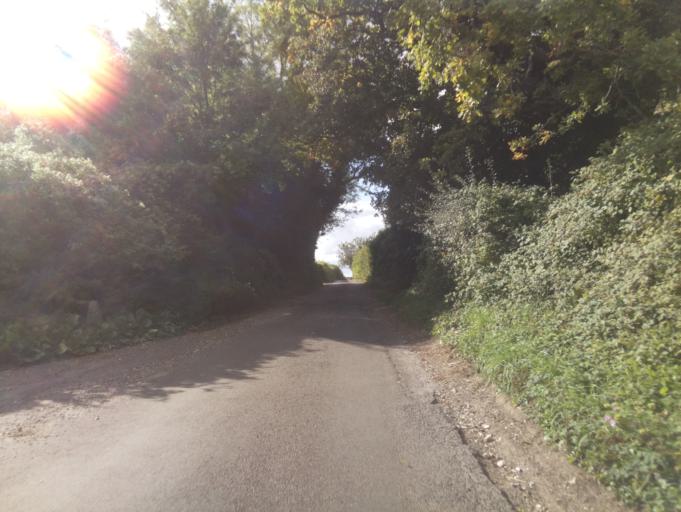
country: GB
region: England
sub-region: Hampshire
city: Chandlers Ford
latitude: 51.0537
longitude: -1.3781
